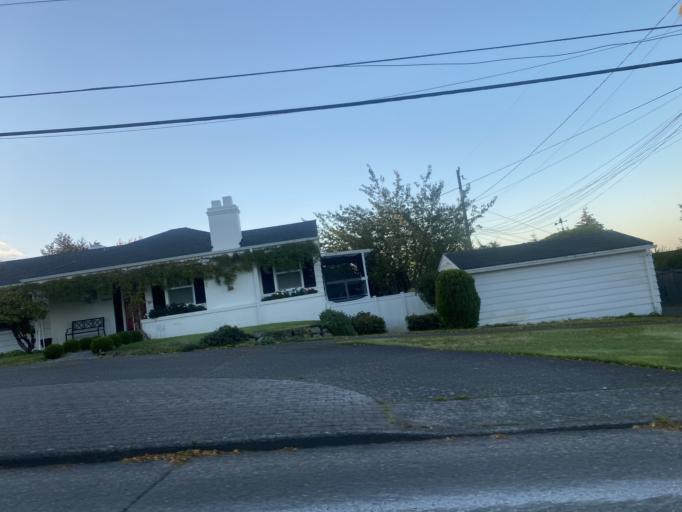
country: US
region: Washington
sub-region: King County
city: Seattle
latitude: 47.6487
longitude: -122.3947
